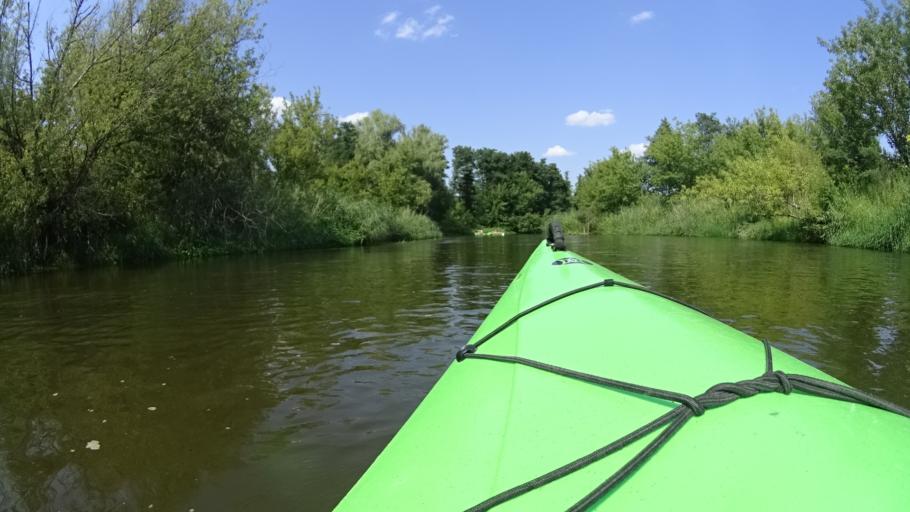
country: PL
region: Masovian Voivodeship
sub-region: Powiat bialobrzeski
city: Wysmierzyce
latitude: 51.6595
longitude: 20.8583
